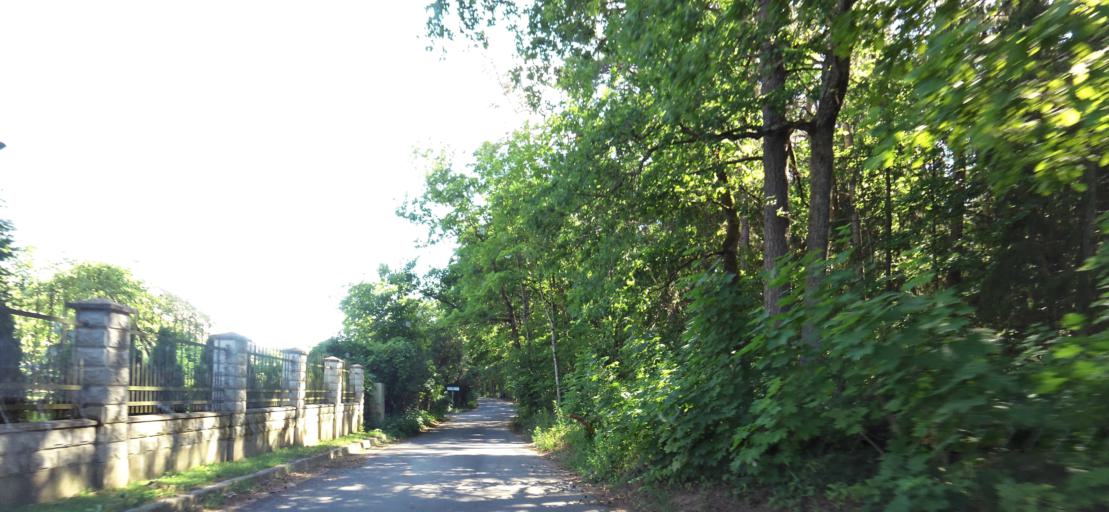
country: LT
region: Vilnius County
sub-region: Vilnius
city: Fabijoniskes
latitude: 54.8245
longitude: 25.3196
